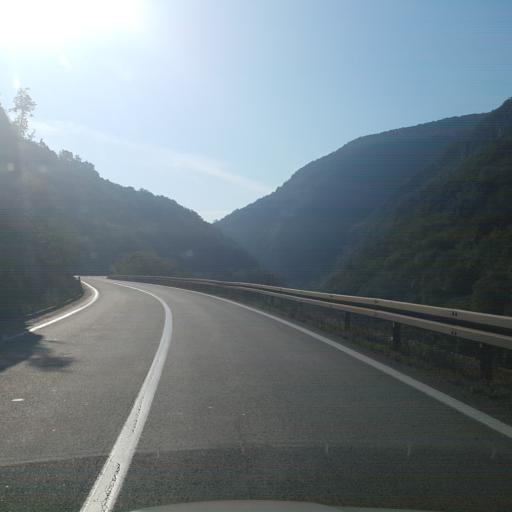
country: RS
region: Central Serbia
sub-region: Nisavski Okrug
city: Svrljig
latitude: 43.3325
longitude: 22.0959
